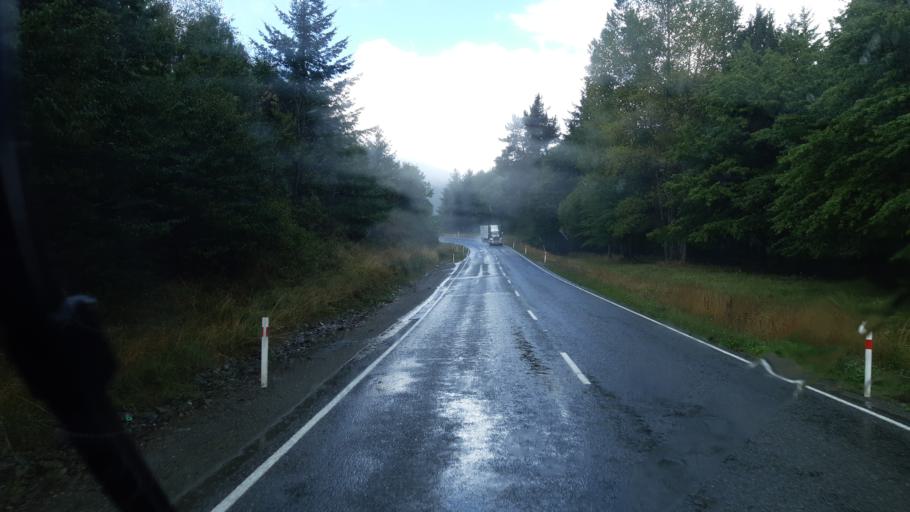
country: NZ
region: Tasman
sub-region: Tasman District
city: Wakefield
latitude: -41.4871
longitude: 172.8907
